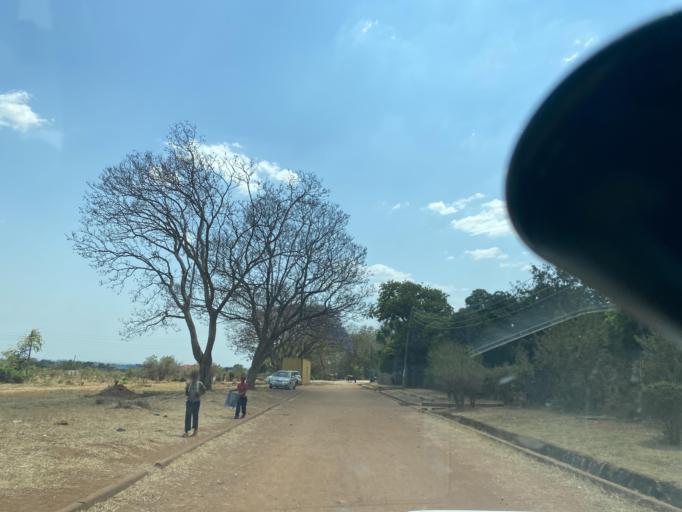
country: ZM
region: Lusaka
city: Kafue
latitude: -15.5063
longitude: 27.9378
